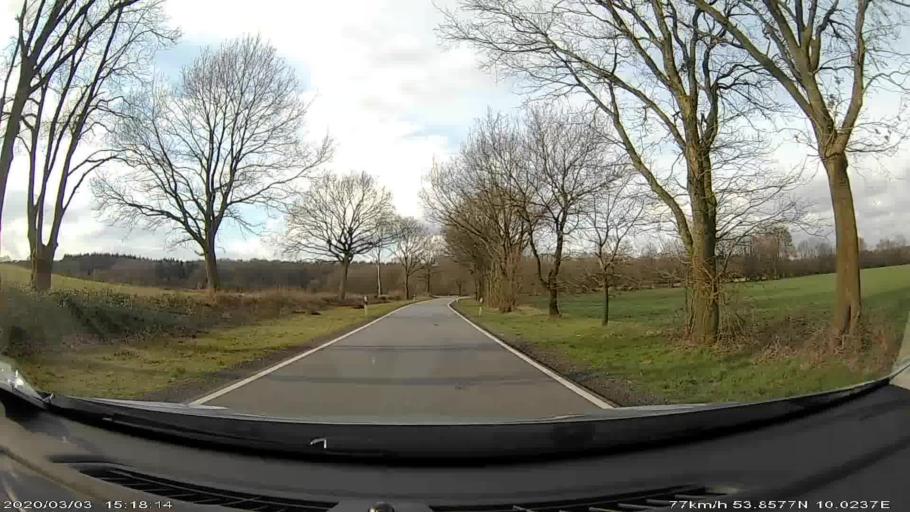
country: DE
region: Schleswig-Holstein
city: Kattendorf
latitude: 53.8573
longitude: 10.0244
